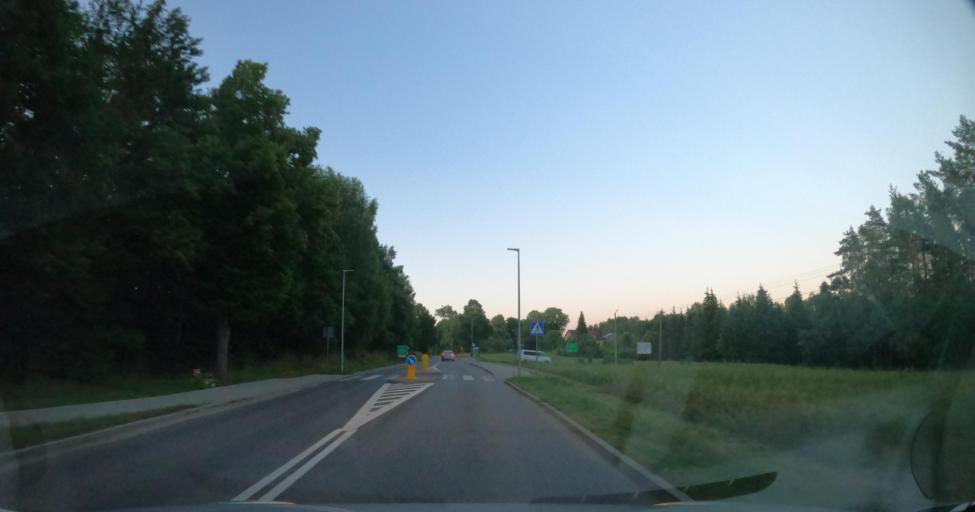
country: PL
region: Pomeranian Voivodeship
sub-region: Powiat wejherowski
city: Luzino
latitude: 54.4623
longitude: 18.0576
